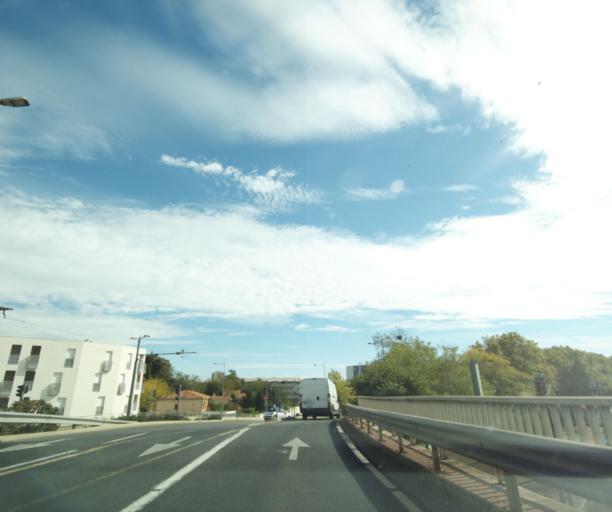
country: FR
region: Languedoc-Roussillon
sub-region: Departement de l'Herault
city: Montpellier
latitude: 43.5960
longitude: 3.8771
